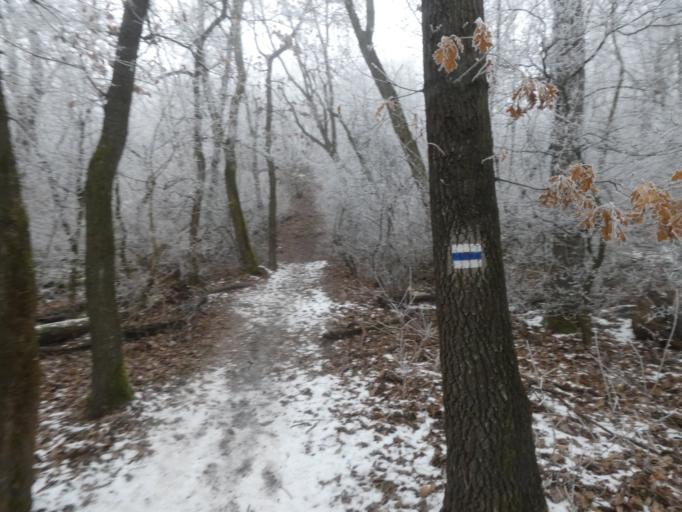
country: HU
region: Pest
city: Urom
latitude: 47.5607
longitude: 18.9946
